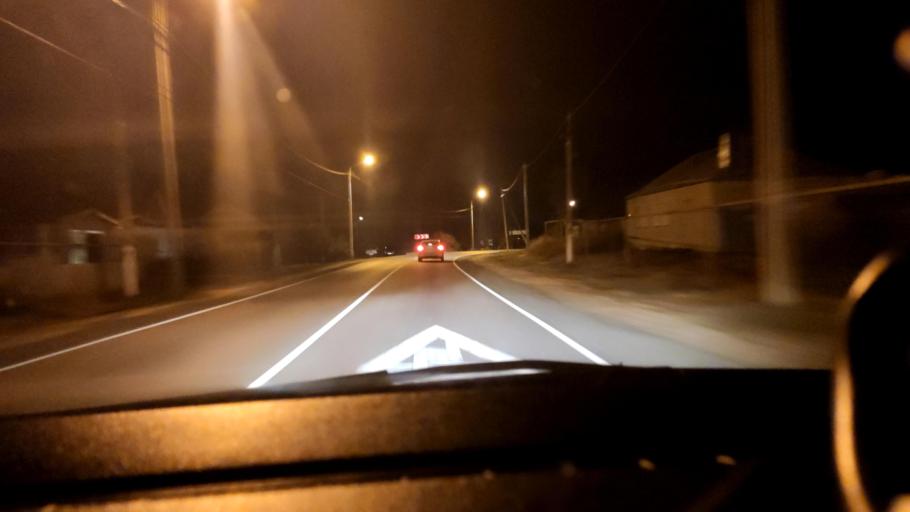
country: RU
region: Voronezj
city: Shilovo
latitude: 51.5771
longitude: 39.0381
